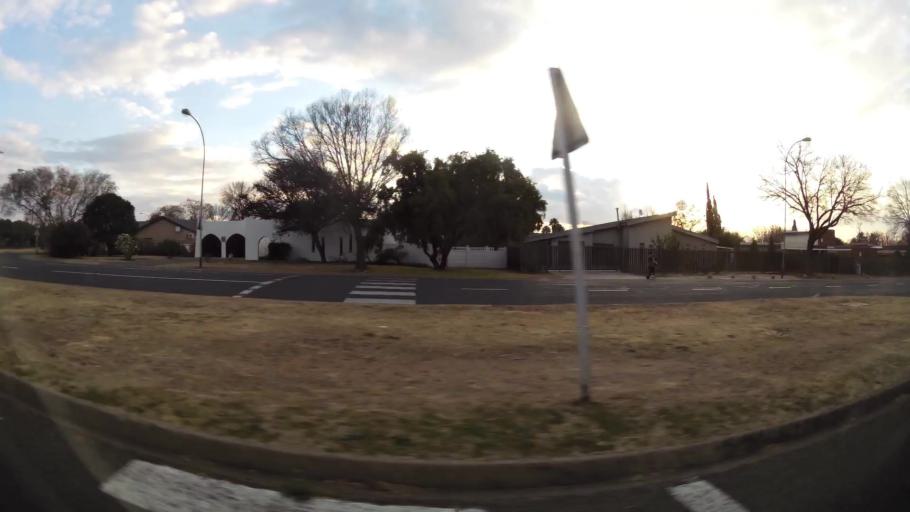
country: ZA
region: Orange Free State
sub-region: Mangaung Metropolitan Municipality
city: Bloemfontein
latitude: -29.1430
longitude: 26.1754
